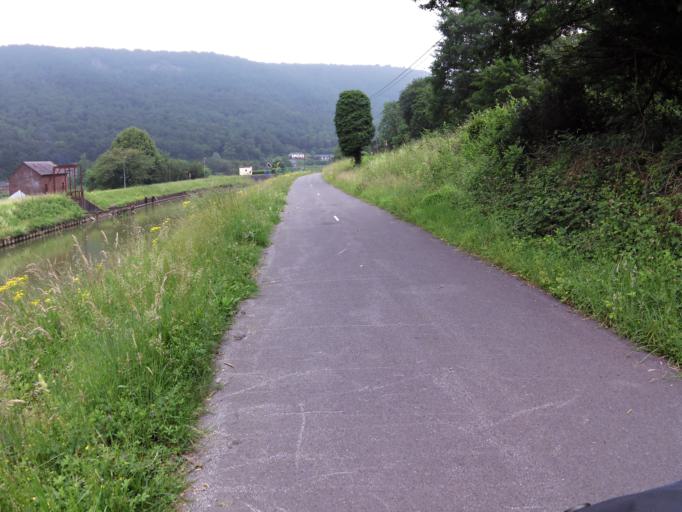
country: FR
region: Champagne-Ardenne
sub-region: Departement des Ardennes
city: Haybes
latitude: 50.0051
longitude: 4.6959
